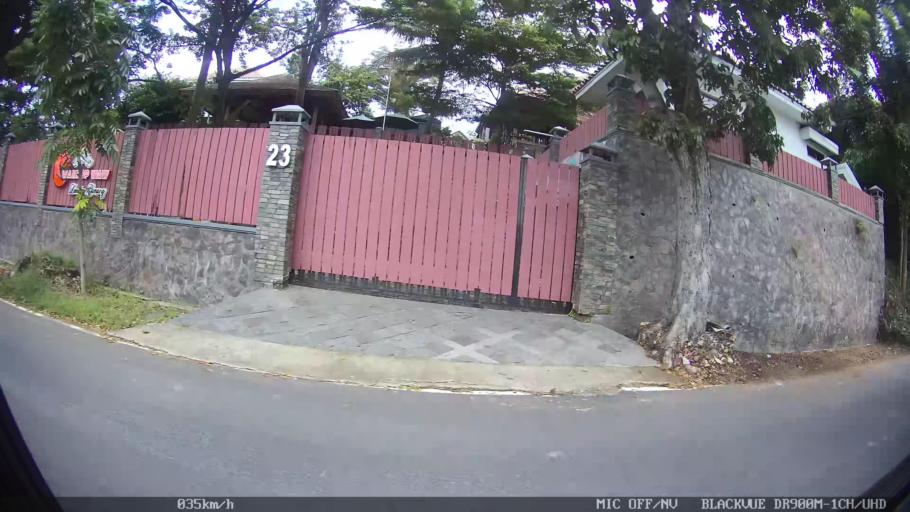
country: ID
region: Lampung
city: Bandarlampung
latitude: -5.4126
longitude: 105.2364
